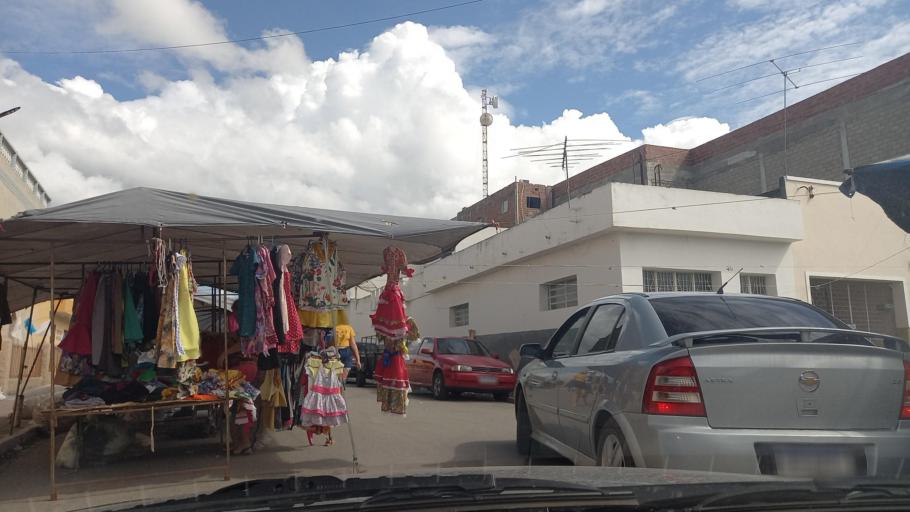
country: BR
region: Pernambuco
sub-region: Cachoeirinha
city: Cachoeirinha
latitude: -8.4879
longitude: -36.2361
